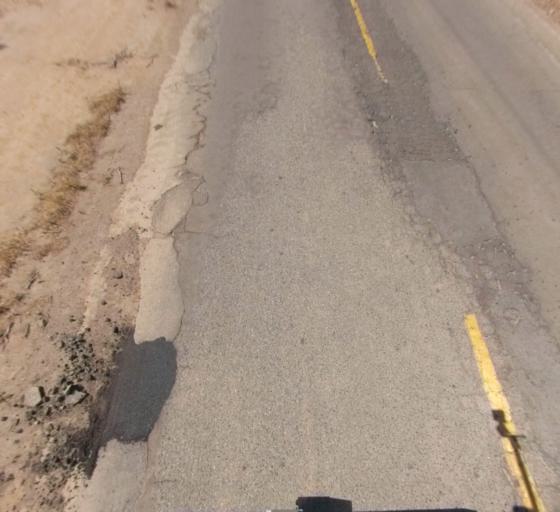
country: US
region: California
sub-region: Madera County
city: Parksdale
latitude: 36.9012
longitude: -119.9393
